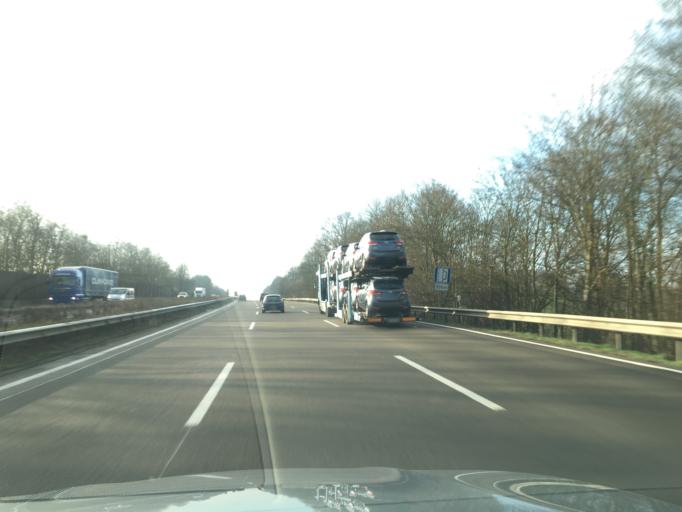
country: DE
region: Rheinland-Pfalz
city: Hohr-Grenzhausen
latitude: 50.4429
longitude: 7.6516
